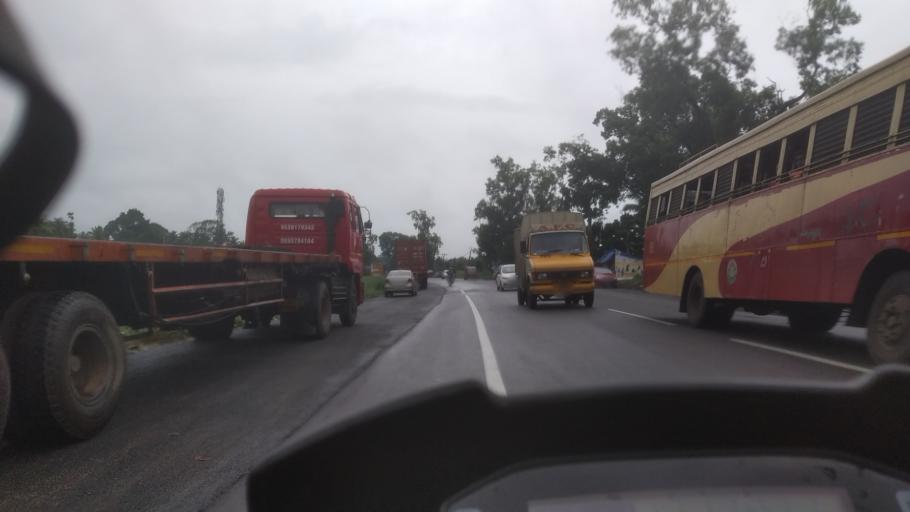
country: IN
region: Kerala
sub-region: Alappuzha
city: Kayankulam
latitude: 9.1468
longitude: 76.5128
